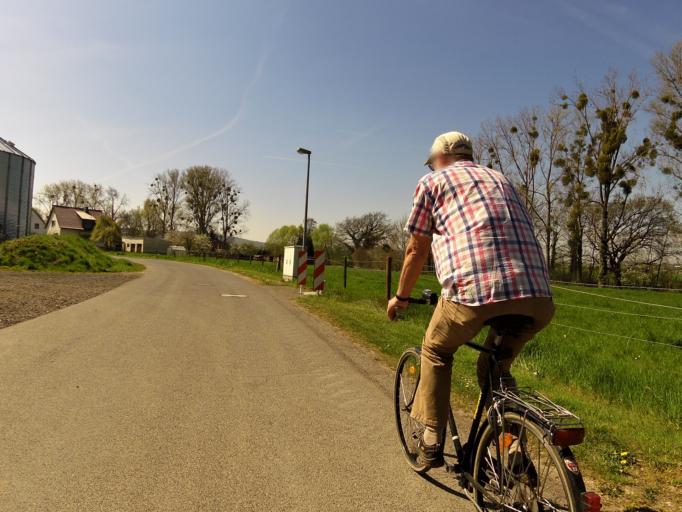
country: DE
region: North Rhine-Westphalia
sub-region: Regierungsbezirk Koln
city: Rheinbach
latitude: 50.6206
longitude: 6.8699
